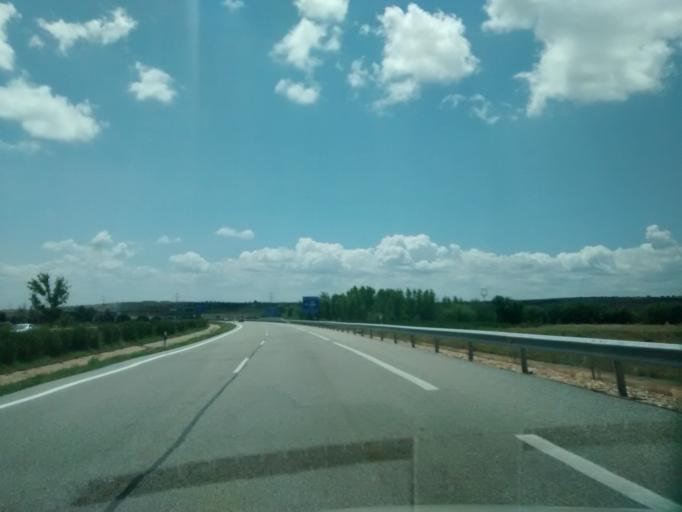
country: ES
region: Castille and Leon
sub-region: Provincia de Leon
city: Astorga
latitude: 42.4580
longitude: -6.0842
